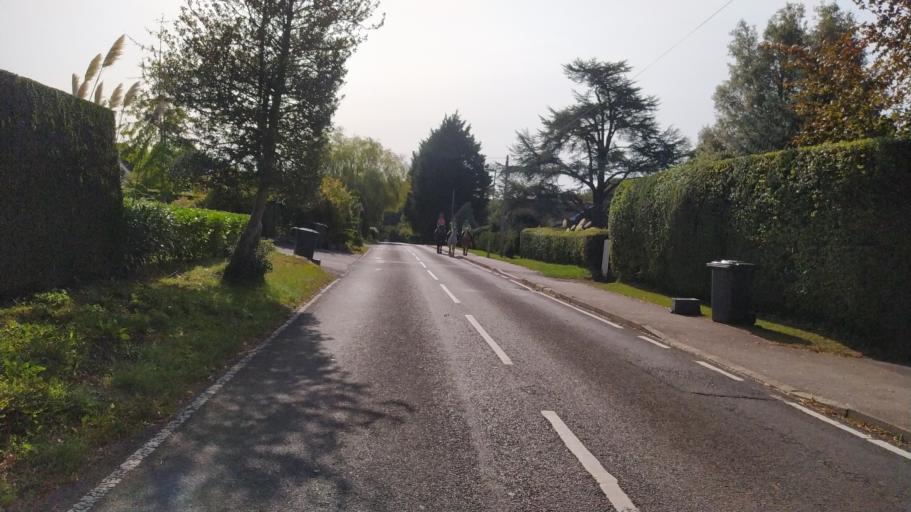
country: GB
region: England
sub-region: Hampshire
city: Havant
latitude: 50.8932
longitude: -0.9600
